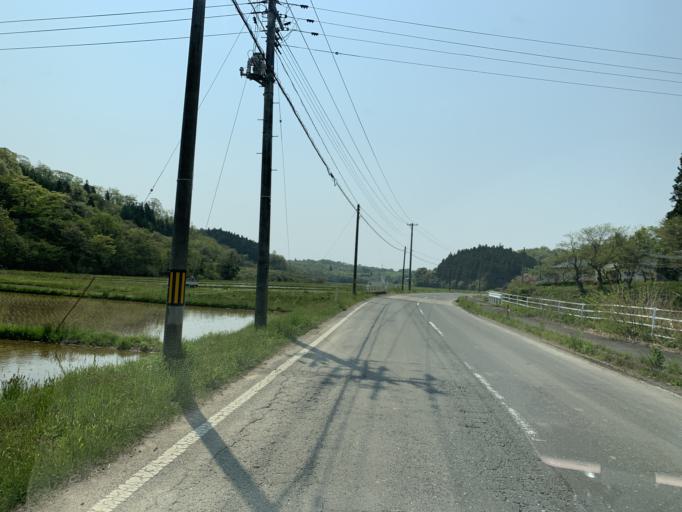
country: JP
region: Iwate
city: Ichinoseki
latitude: 38.8665
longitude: 141.0449
